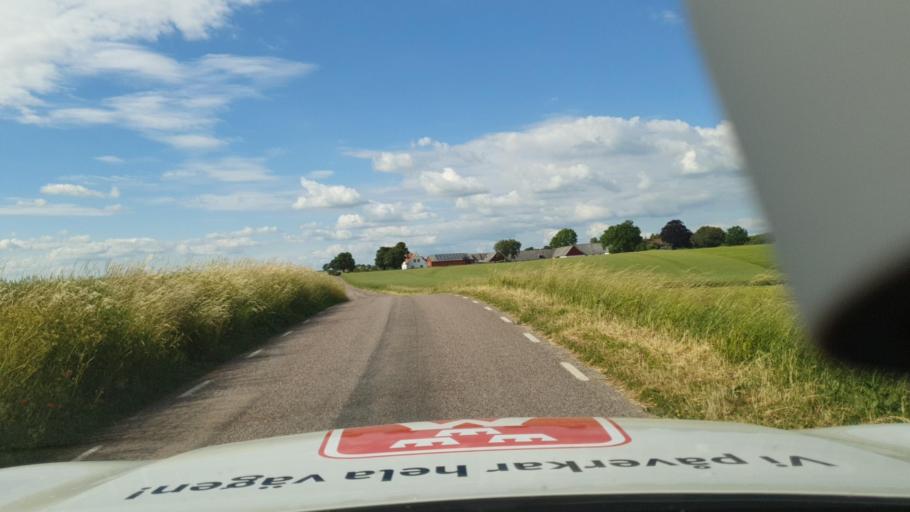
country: SE
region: Skane
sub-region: Skurups Kommun
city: Skurup
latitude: 55.4470
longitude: 13.5191
